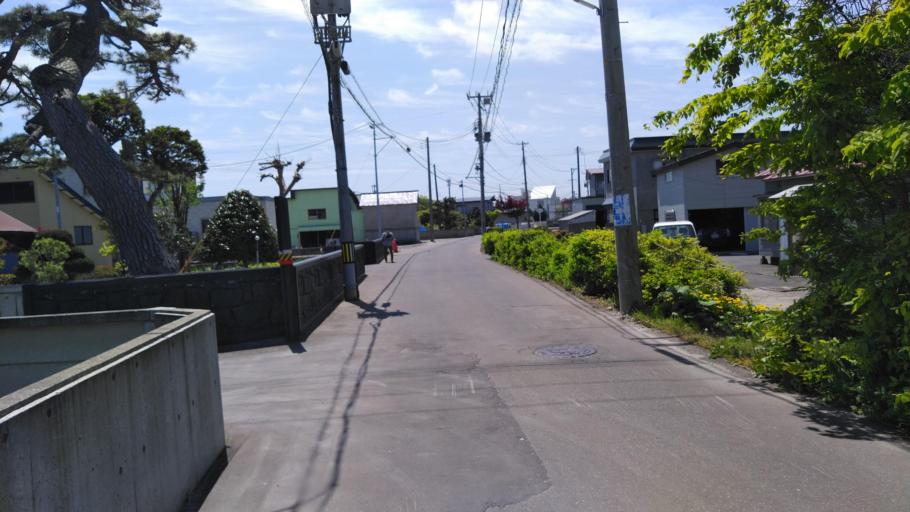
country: JP
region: Aomori
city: Aomori Shi
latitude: 40.8310
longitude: 140.6984
